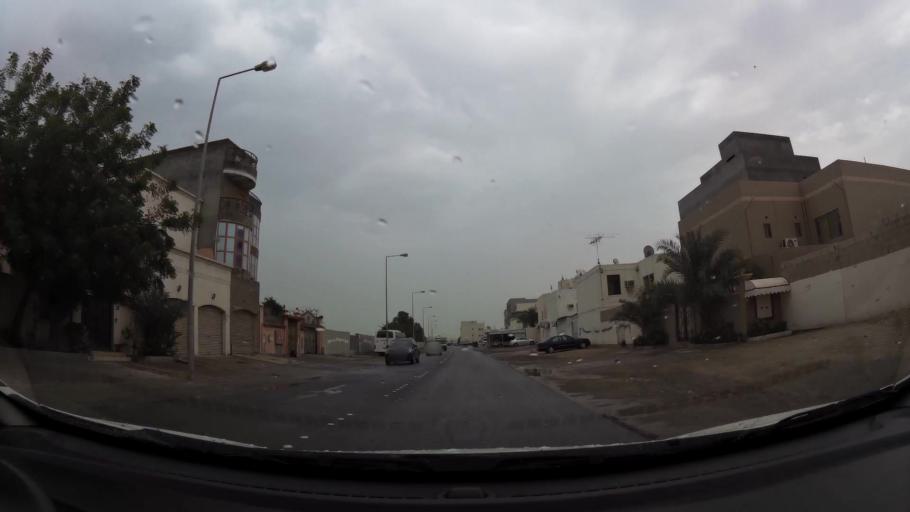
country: BH
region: Northern
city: Madinat `Isa
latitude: 26.1603
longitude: 50.5742
